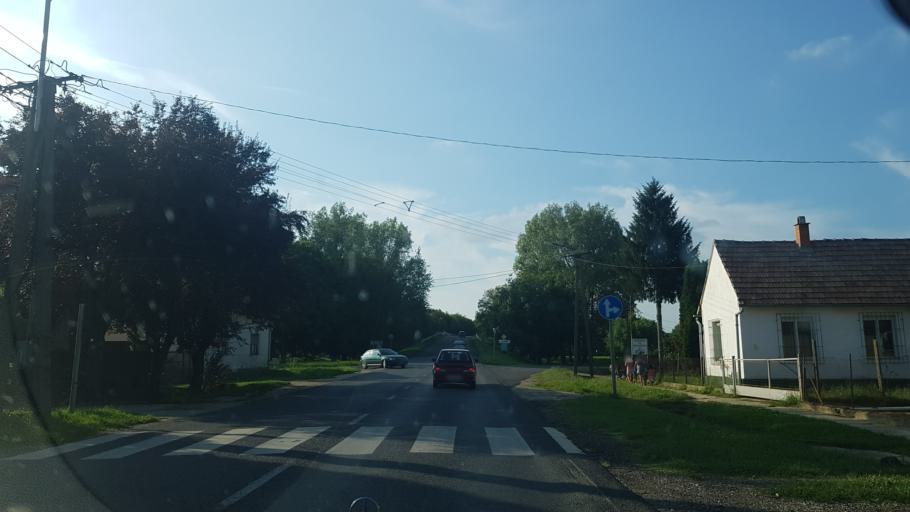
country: HU
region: Somogy
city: Segesd
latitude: 46.2897
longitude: 17.3588
